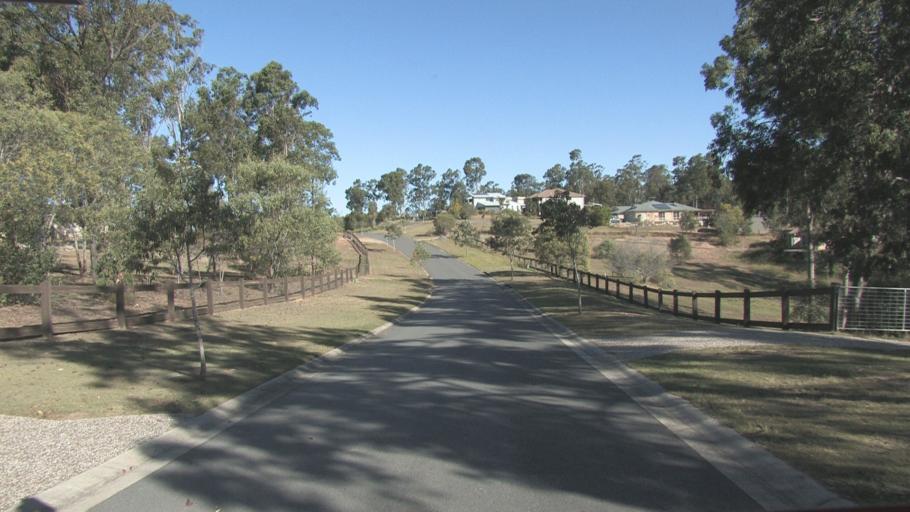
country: AU
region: Queensland
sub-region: Ipswich
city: Springfield Lakes
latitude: -27.7174
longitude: 152.9205
